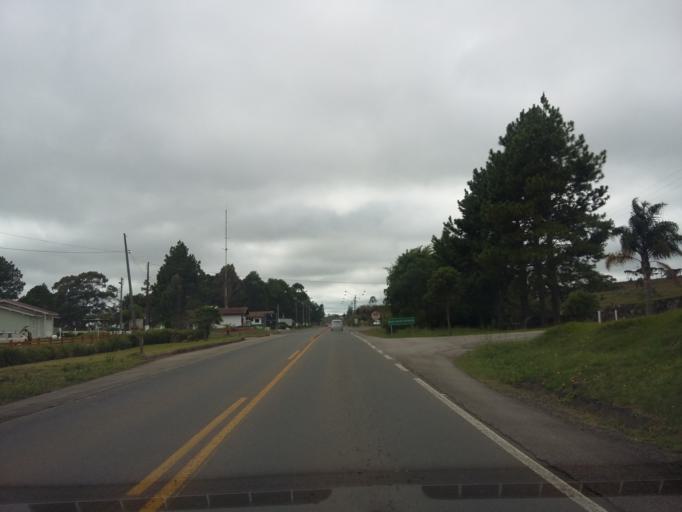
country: BR
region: Santa Catarina
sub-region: Lages
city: Lages
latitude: -27.8907
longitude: -50.1514
